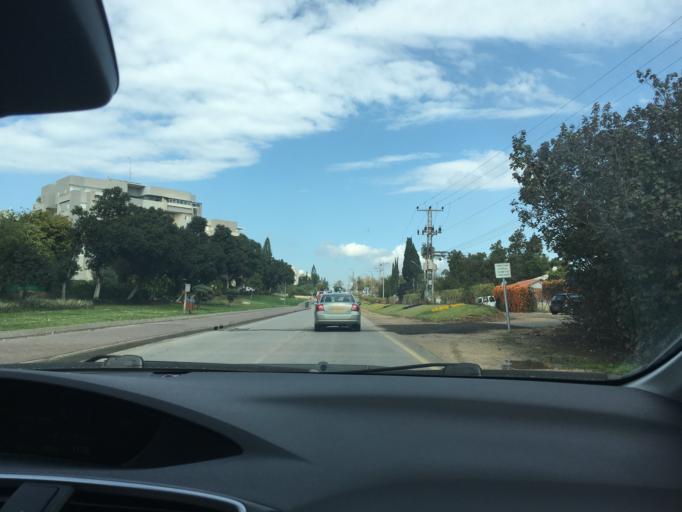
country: IL
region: Tel Aviv
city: Ramat HaSharon
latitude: 32.1636
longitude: 34.8531
